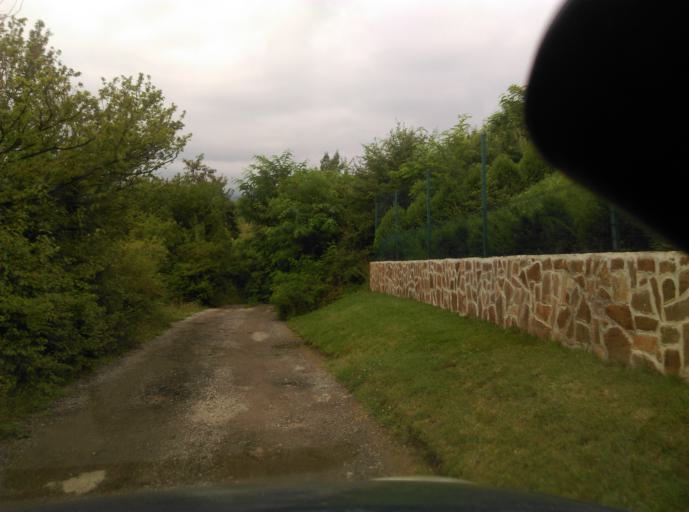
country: BG
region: Sofia-Capital
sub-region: Stolichna Obshtina
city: Sofia
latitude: 42.5881
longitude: 23.3946
